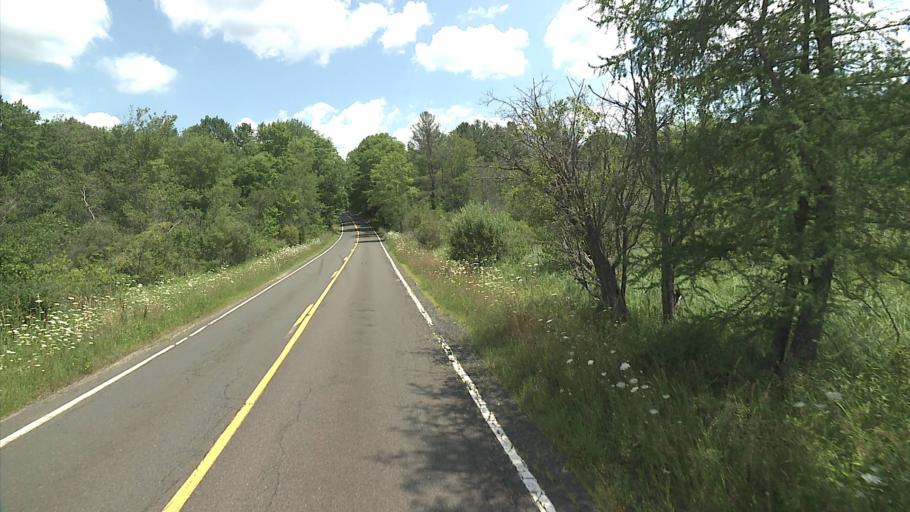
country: US
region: Connecticut
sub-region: Litchfield County
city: Winsted
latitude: 41.9891
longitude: -73.0985
